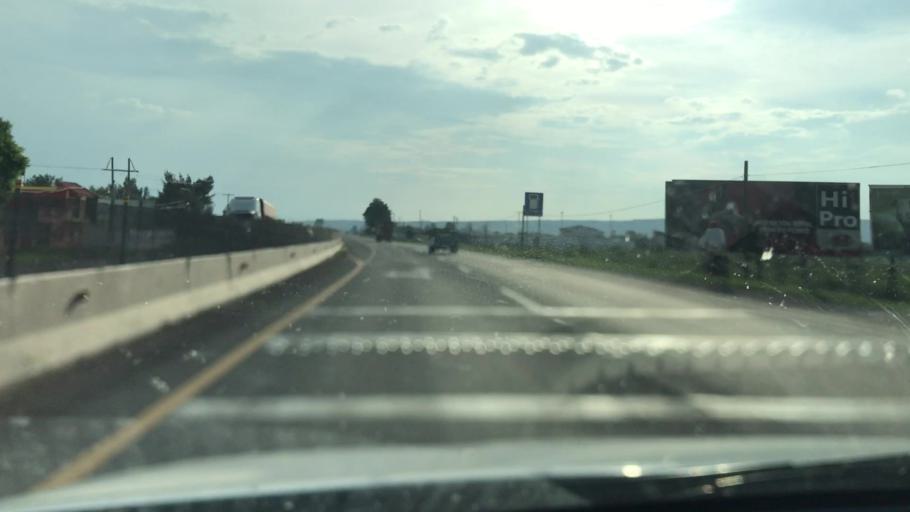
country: MX
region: Guanajuato
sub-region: Penjamo
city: Estacion la Piedad
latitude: 20.3893
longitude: -101.9256
